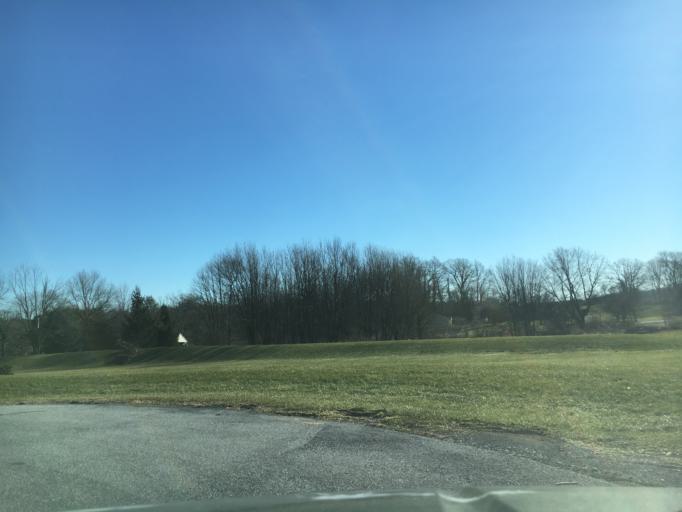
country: US
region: Pennsylvania
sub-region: Berks County
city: Fleetwood
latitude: 40.4271
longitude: -75.8280
